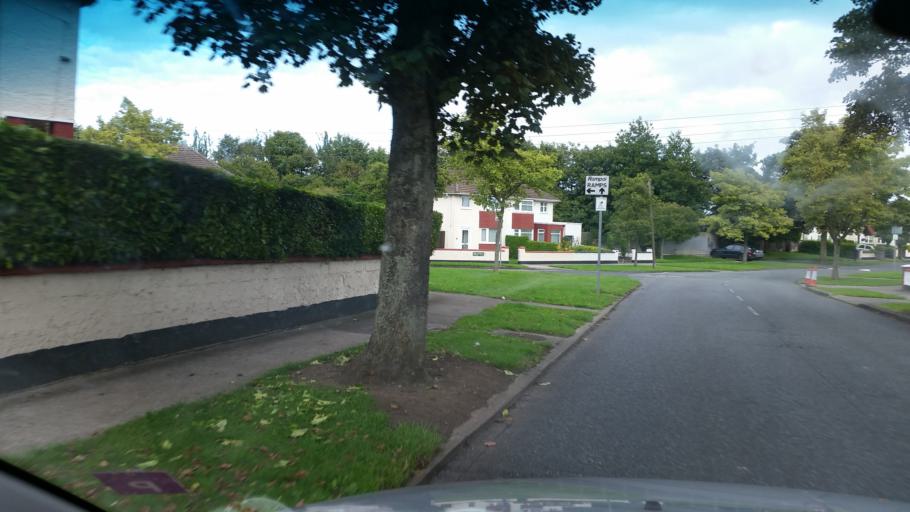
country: IE
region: Leinster
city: Beaumont
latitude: 53.3911
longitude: -6.2514
